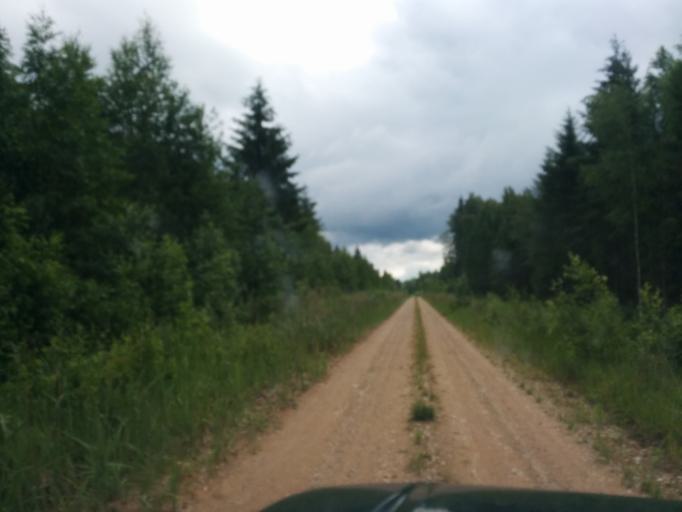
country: LV
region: Vilaka
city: Vilaka
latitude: 57.3933
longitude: 27.6236
